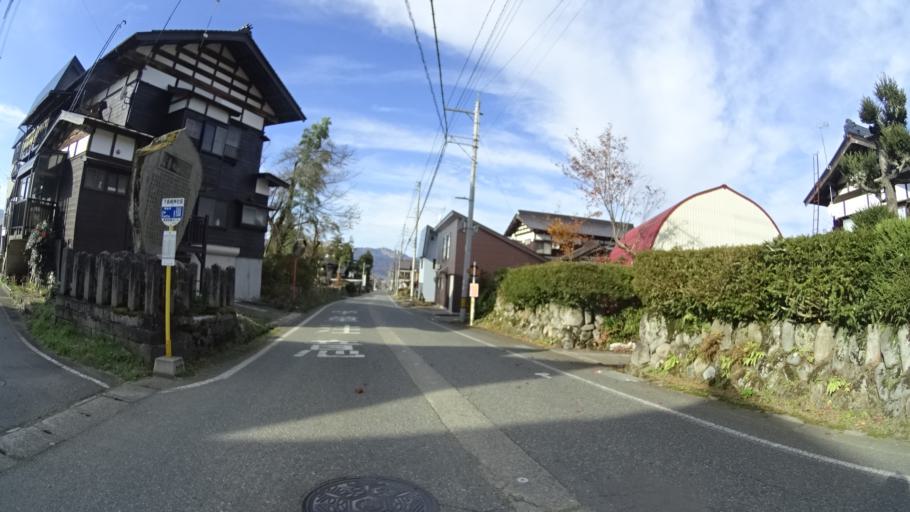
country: JP
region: Niigata
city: Shiozawa
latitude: 37.0149
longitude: 138.8796
